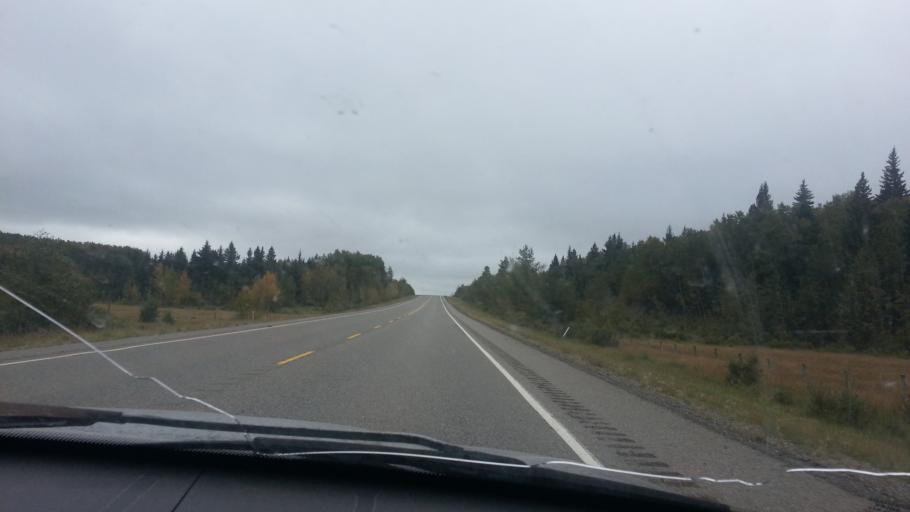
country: CA
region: Alberta
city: Cochrane
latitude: 51.0659
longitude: -114.6992
